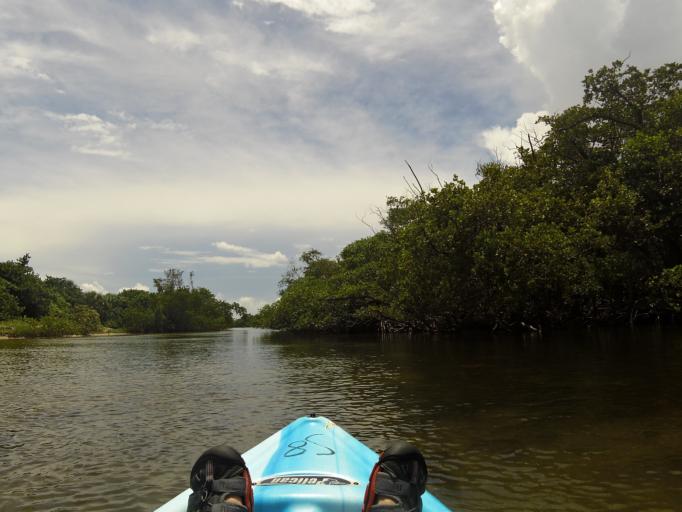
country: US
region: Florida
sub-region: Broward County
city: Dania Beach
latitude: 26.0756
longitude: -80.1110
